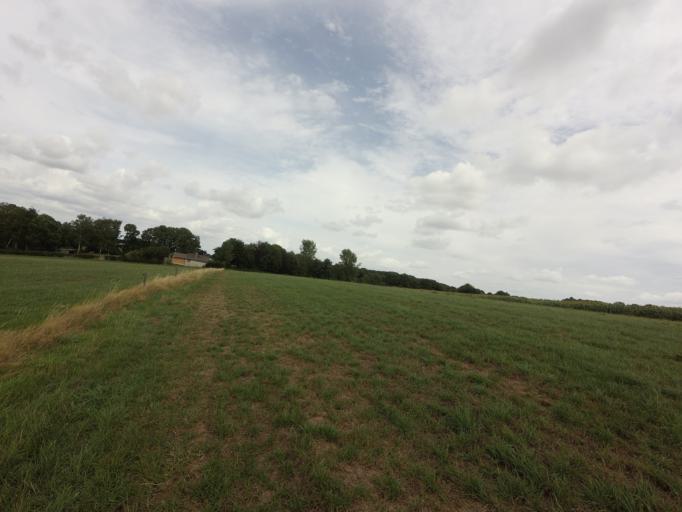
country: NL
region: Limburg
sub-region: Valkenburg aan de Geul
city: Schin op Geul
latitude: 50.7909
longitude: 5.8872
